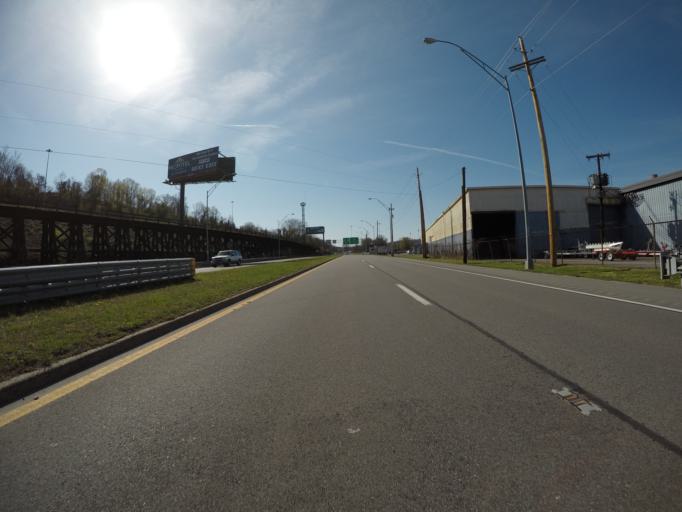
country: US
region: West Virginia
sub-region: Kanawha County
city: South Charleston
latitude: 38.3620
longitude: -81.6660
